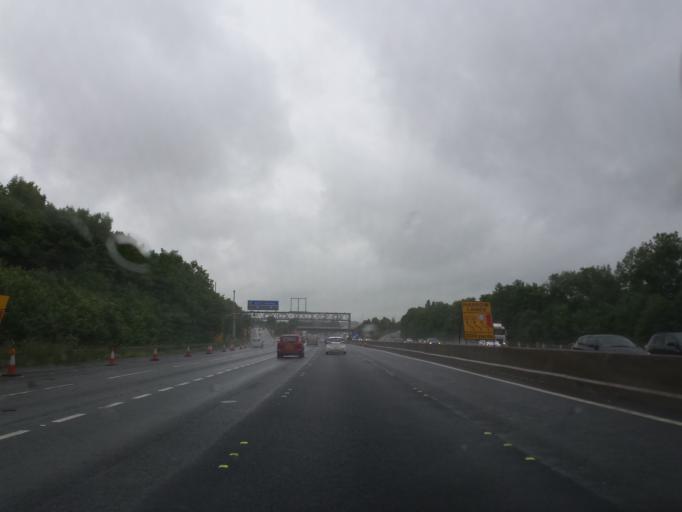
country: GB
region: England
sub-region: Rotherham
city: Ulley
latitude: 53.3671
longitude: -1.2829
